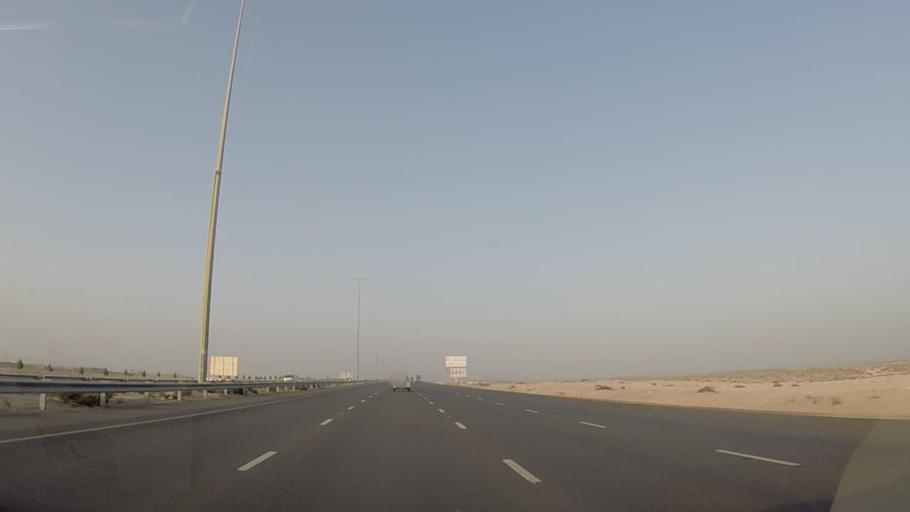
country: AE
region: Dubai
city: Dubai
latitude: 24.9392
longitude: 55.0393
